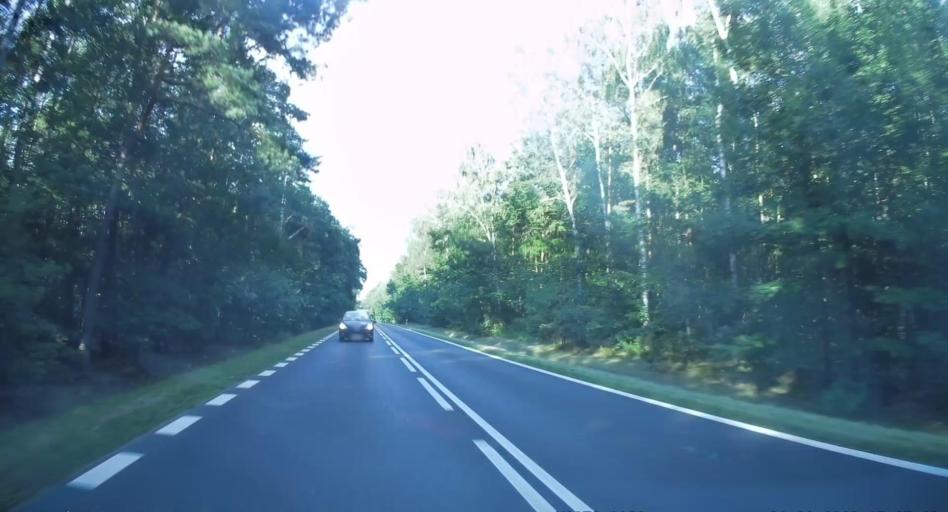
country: PL
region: Lodz Voivodeship
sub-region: Powiat rawski
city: Rawa Mazowiecka
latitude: 51.7805
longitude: 20.3097
